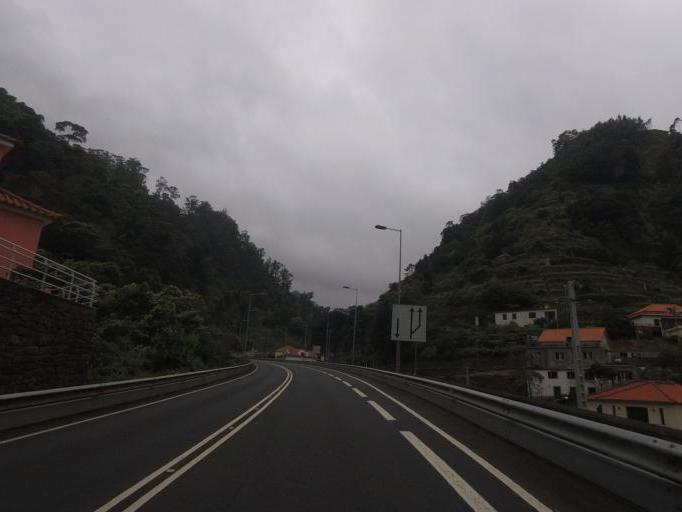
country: PT
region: Madeira
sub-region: Santa Cruz
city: Santa Cruz
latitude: 32.7349
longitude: -16.8055
